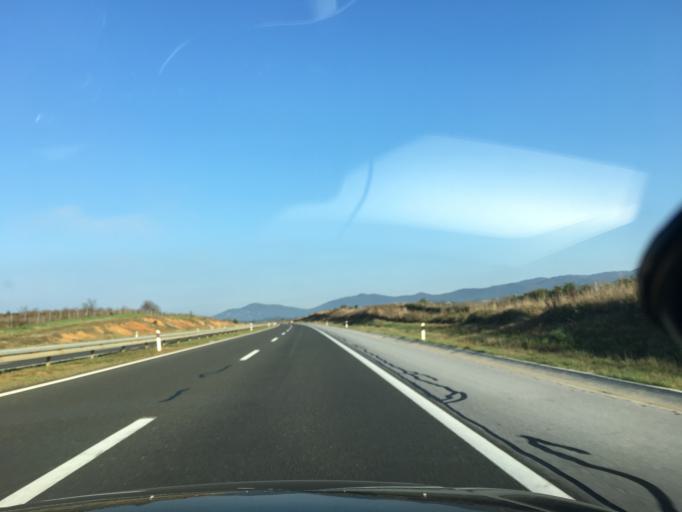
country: HR
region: Licko-Senjska
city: Gospic
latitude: 44.4970
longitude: 15.5357
